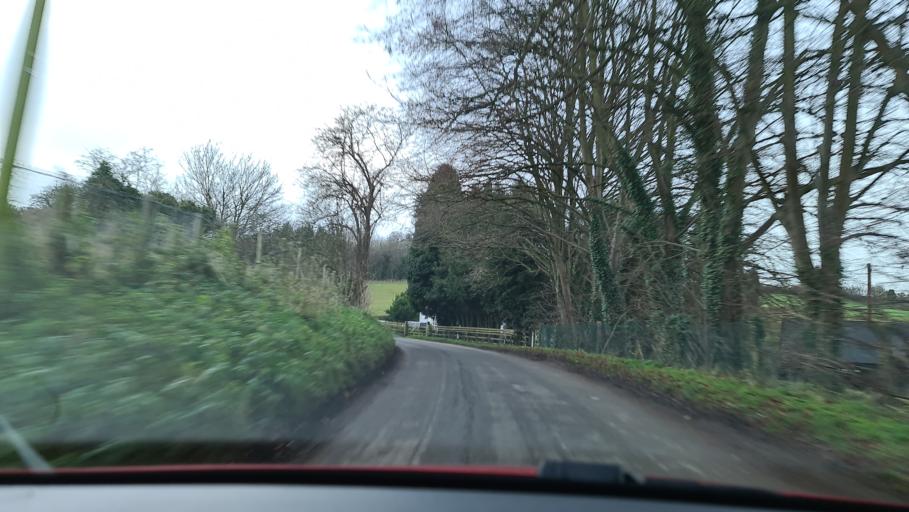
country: GB
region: England
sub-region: Buckinghamshire
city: Princes Risborough
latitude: 51.7157
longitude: -0.8139
